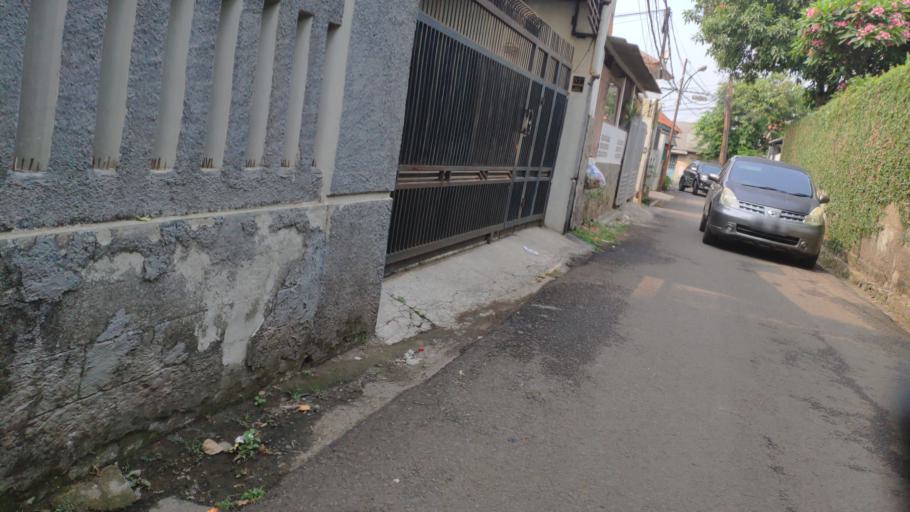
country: ID
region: West Java
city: Depok
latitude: -6.3443
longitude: 106.8081
